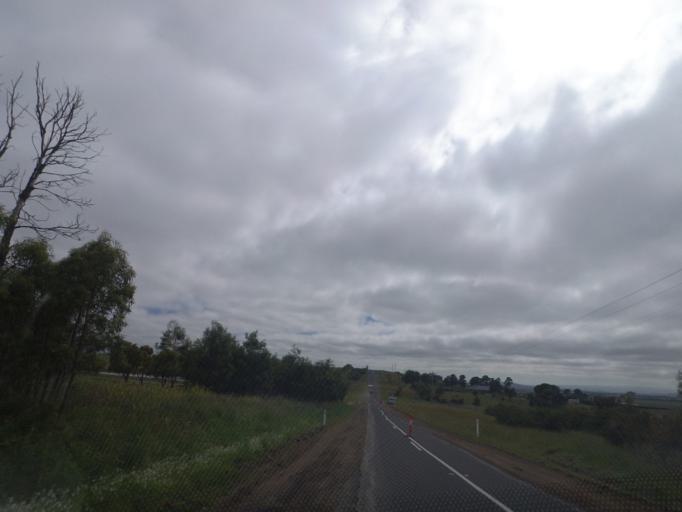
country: AU
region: Victoria
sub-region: Hume
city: Craigieburn
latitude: -37.5272
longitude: 144.8886
